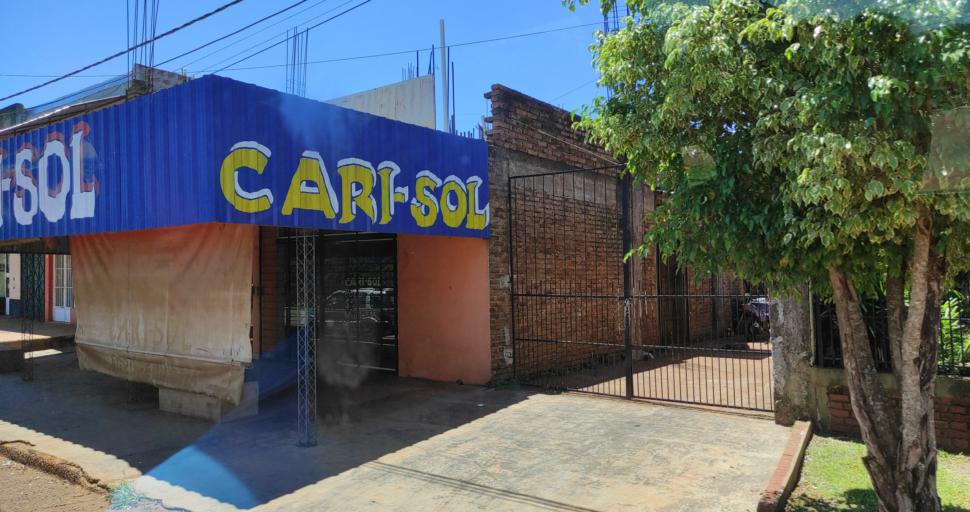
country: AR
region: Misiones
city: Dos de Mayo
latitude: -26.9902
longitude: -54.4785
